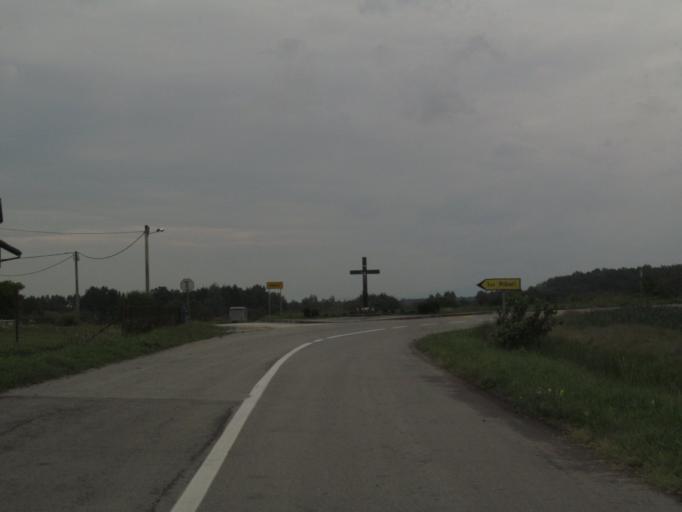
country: HR
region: Karlovacka
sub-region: Grad Karlovac
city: Karlovac
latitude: 45.4880
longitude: 15.6975
